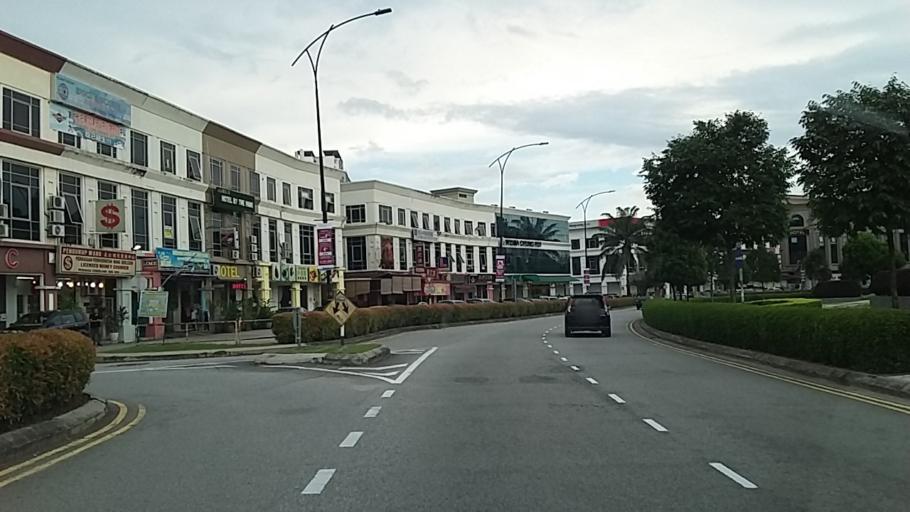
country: MY
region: Johor
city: Skudai
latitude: 1.4815
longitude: 103.6591
